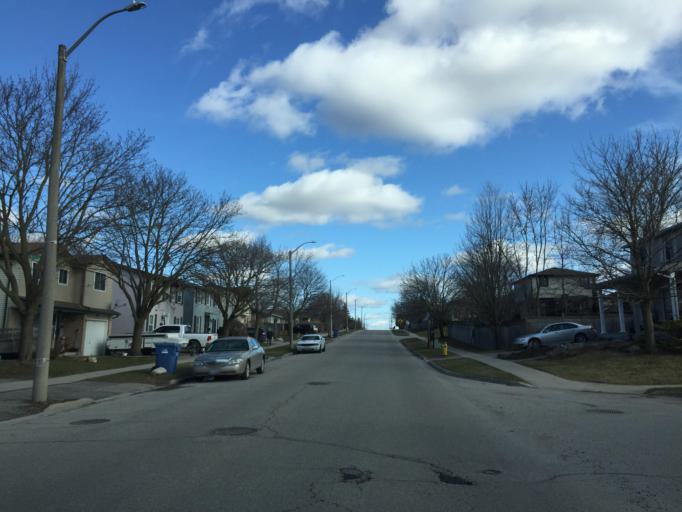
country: CA
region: Ontario
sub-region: Wellington County
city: Guelph
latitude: 43.5137
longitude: -80.2804
